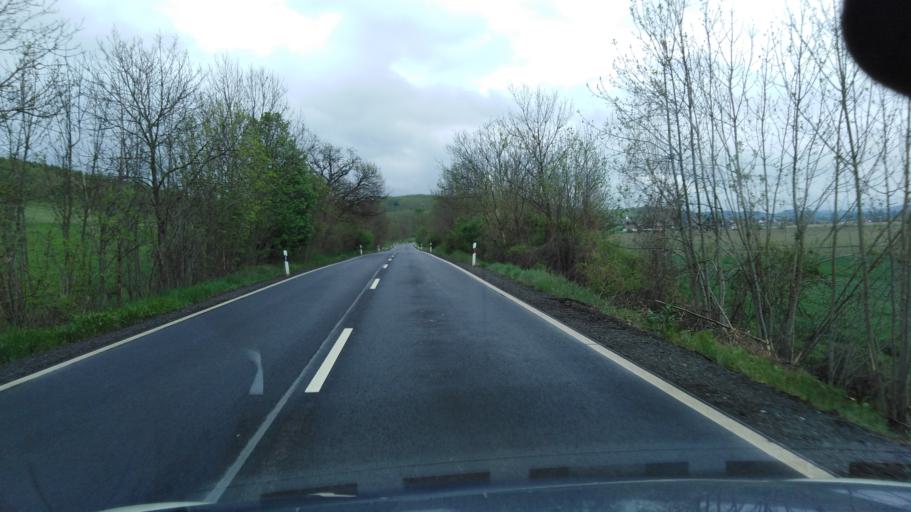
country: HU
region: Nograd
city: Karancskeszi
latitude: 48.1291
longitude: 19.6225
